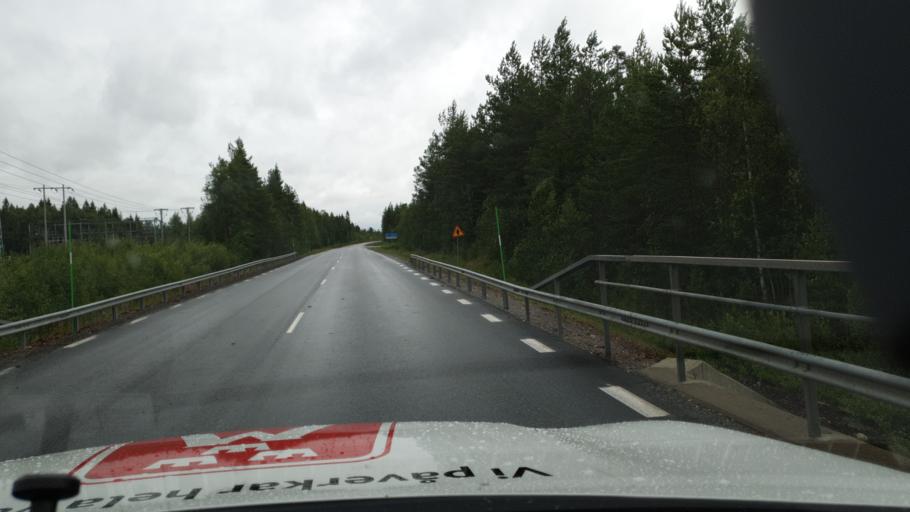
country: SE
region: Vaesterbotten
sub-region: Umea Kommun
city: Saevar
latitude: 63.9079
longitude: 20.5280
